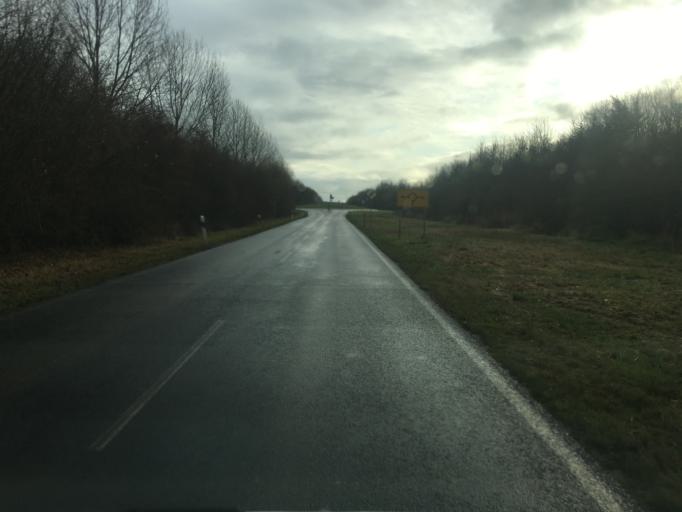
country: DE
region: North Rhine-Westphalia
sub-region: Regierungsbezirk Koln
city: Inden
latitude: 50.8446
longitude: 6.4157
